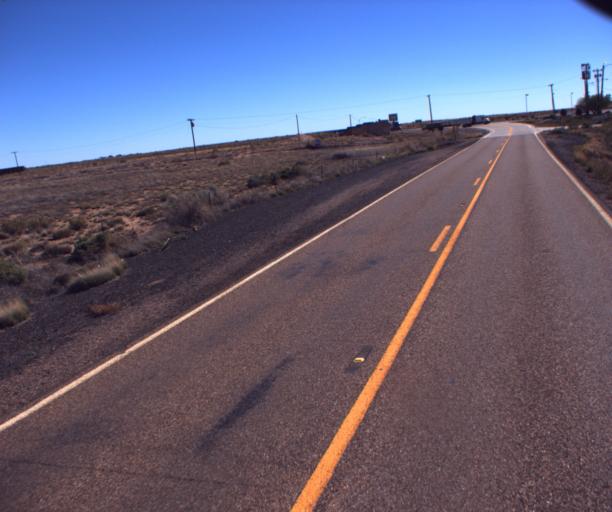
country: US
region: Arizona
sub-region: Navajo County
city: Holbrook
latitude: 34.9778
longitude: -110.0885
